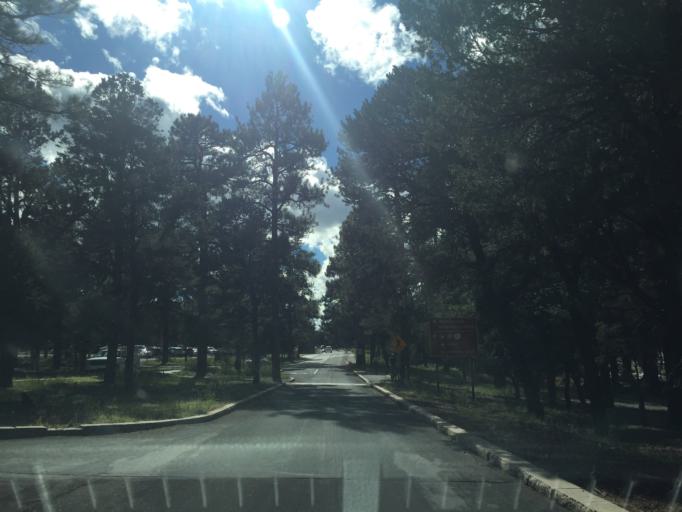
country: US
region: Arizona
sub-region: Coconino County
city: Grand Canyon
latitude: 36.0558
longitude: -112.1375
